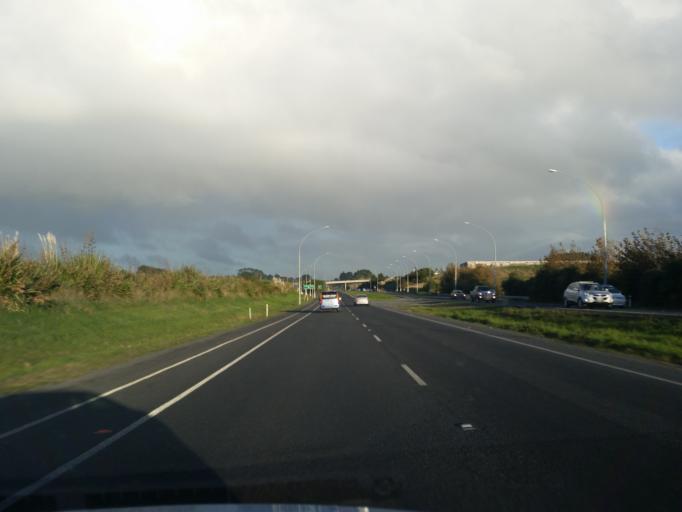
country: NZ
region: Waikato
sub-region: Waikato District
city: Te Kauwhata
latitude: -37.3504
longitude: 175.0791
